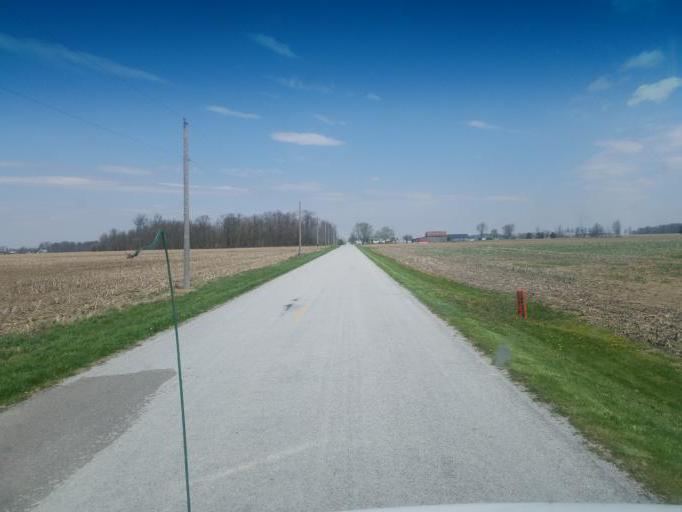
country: US
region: Ohio
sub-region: Hardin County
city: Forest
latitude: 40.7401
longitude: -83.5377
